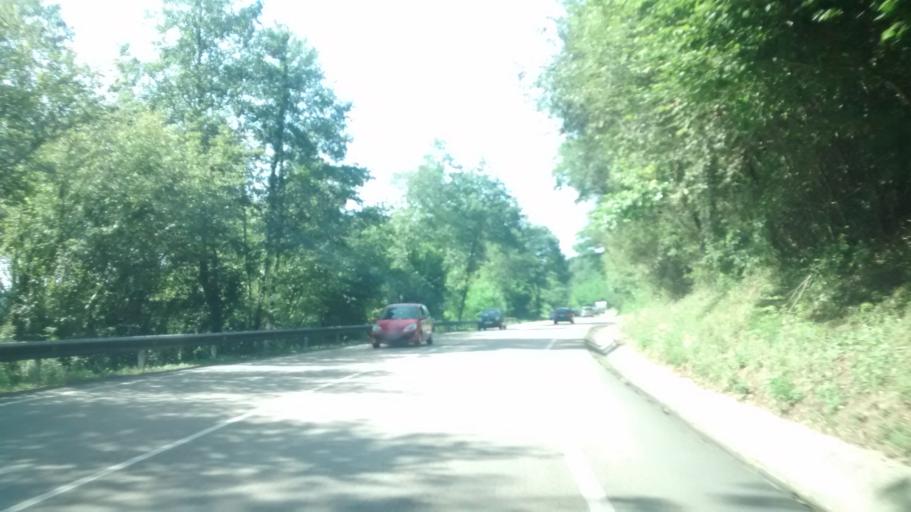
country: ES
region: Cantabria
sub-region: Provincia de Cantabria
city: Hazas de Cesto
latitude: 43.4287
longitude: -3.5665
